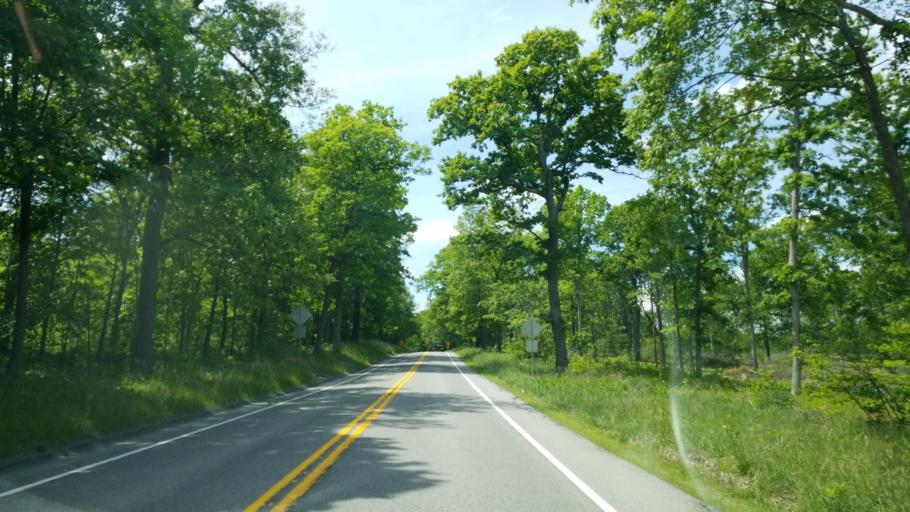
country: US
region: Pennsylvania
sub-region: Blair County
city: Tipton
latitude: 40.7053
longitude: -78.3102
